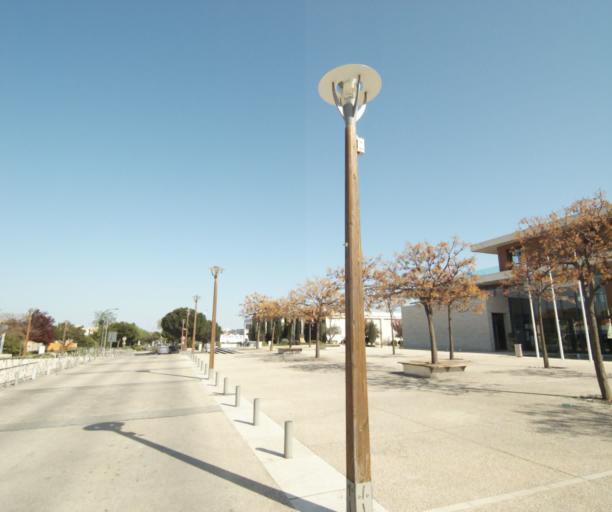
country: FR
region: Languedoc-Roussillon
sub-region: Departement de l'Herault
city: Juvignac
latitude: 43.6139
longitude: 3.8048
